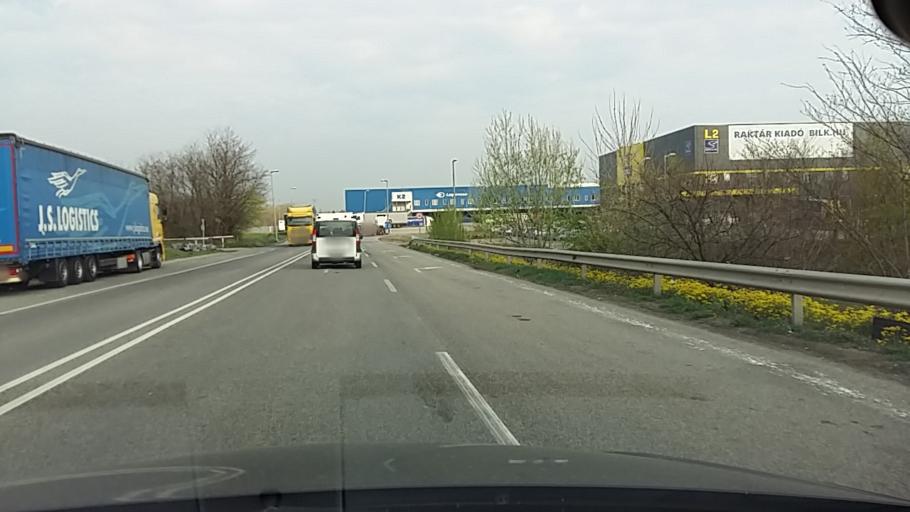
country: HU
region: Pest
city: Dunaharaszti
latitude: 47.3706
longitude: 19.1168
